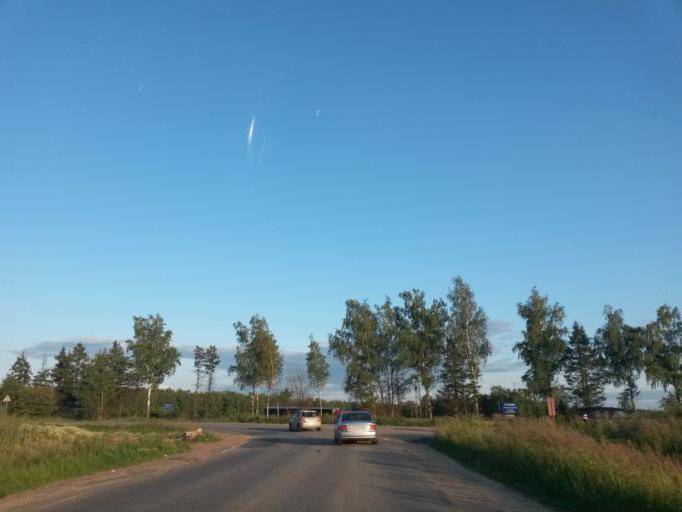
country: RU
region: Moskovskaya
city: Vostryakovo
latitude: 55.3341
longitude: 37.7386
